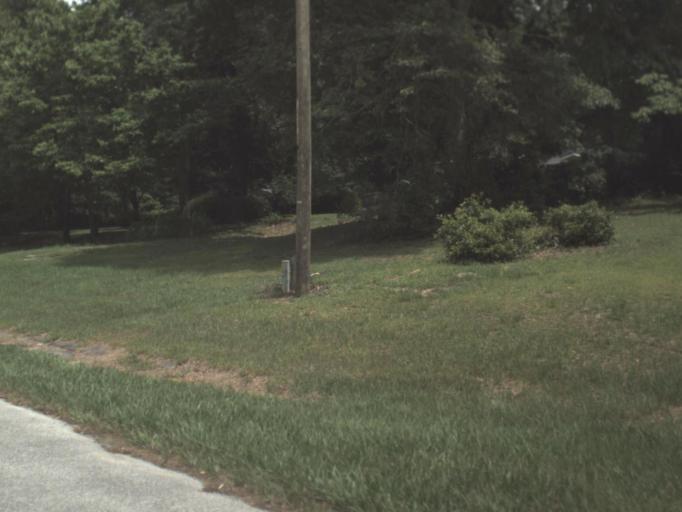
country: US
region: Florida
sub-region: Madison County
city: Madison
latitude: 30.4723
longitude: -83.3518
